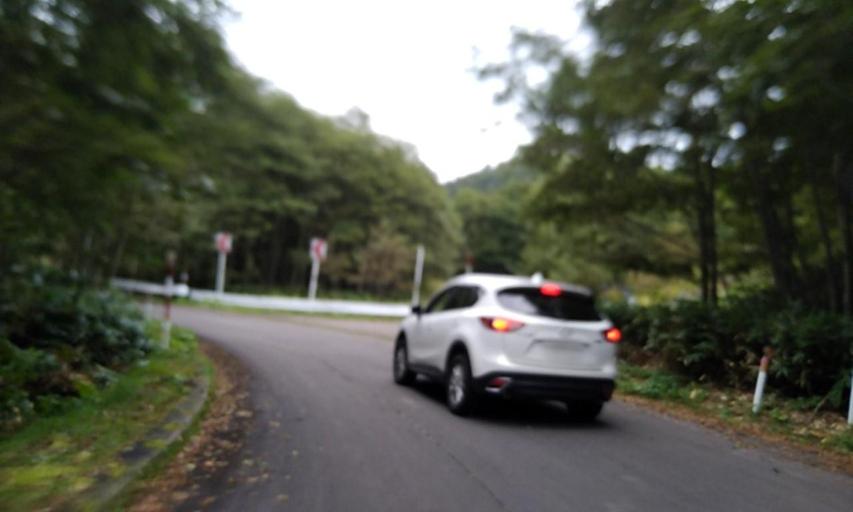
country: JP
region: Hokkaido
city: Bihoro
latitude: 43.5721
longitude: 144.2009
